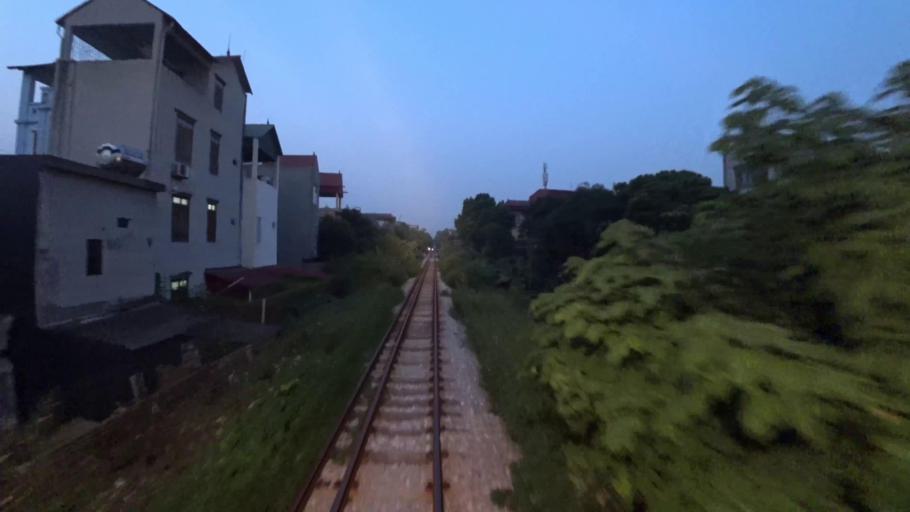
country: VN
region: Ha Noi
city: Soc Son
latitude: 21.2518
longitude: 105.8617
